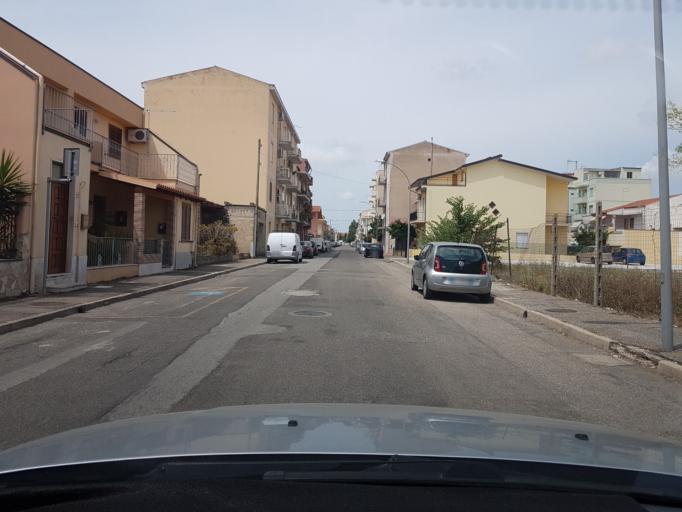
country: IT
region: Sardinia
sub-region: Provincia di Oristano
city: Oristano
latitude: 39.9101
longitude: 8.5959
